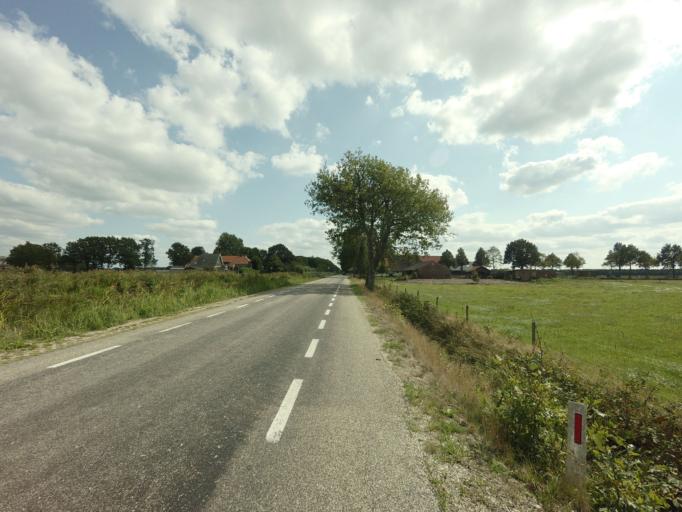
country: NL
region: Drenthe
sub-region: Gemeente Westerveld
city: Dwingeloo
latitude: 52.8722
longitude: 6.4406
